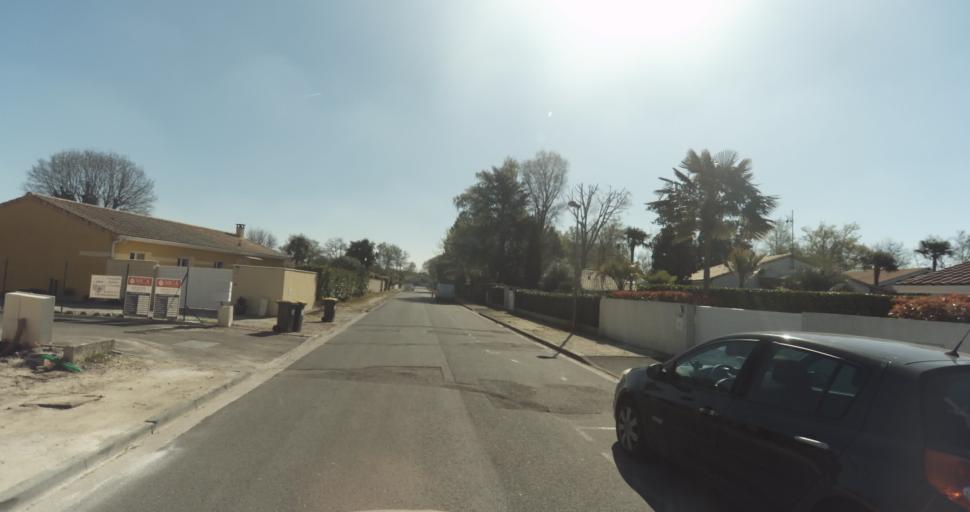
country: FR
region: Aquitaine
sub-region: Departement de la Gironde
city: Martignas-sur-Jalle
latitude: 44.8019
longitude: -0.7860
